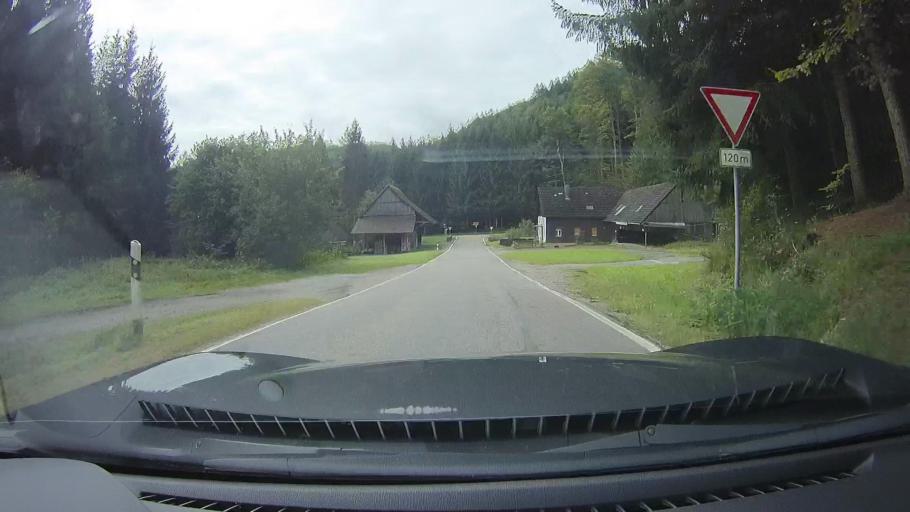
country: DE
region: Baden-Wuerttemberg
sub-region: Regierungsbezirk Stuttgart
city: Lowenstein
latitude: 49.0720
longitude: 9.4250
